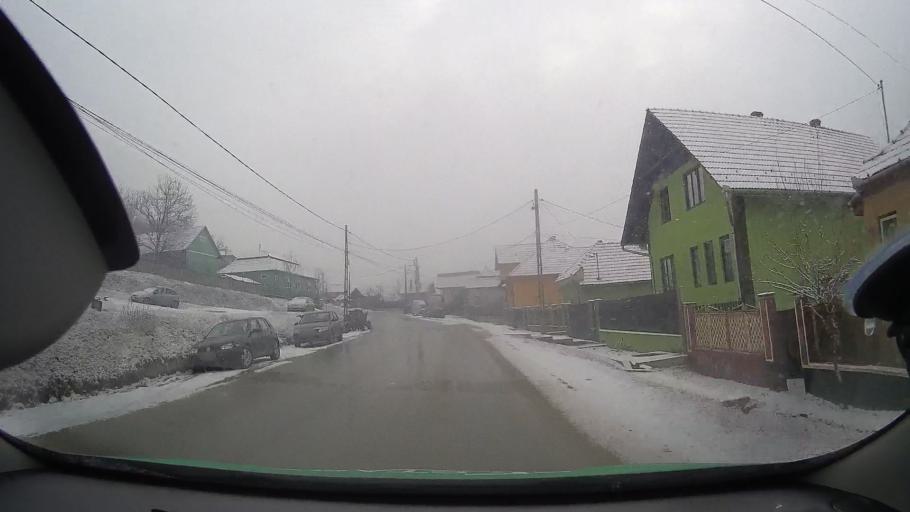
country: RO
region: Alba
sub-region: Comuna Lopadea Noua
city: Lopadea Noua
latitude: 46.2950
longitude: 23.8155
